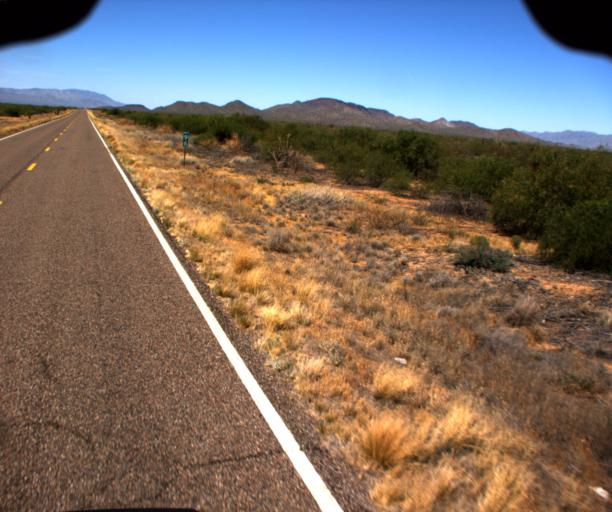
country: US
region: Arizona
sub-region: Yavapai County
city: Congress
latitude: 34.0625
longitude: -113.0433
